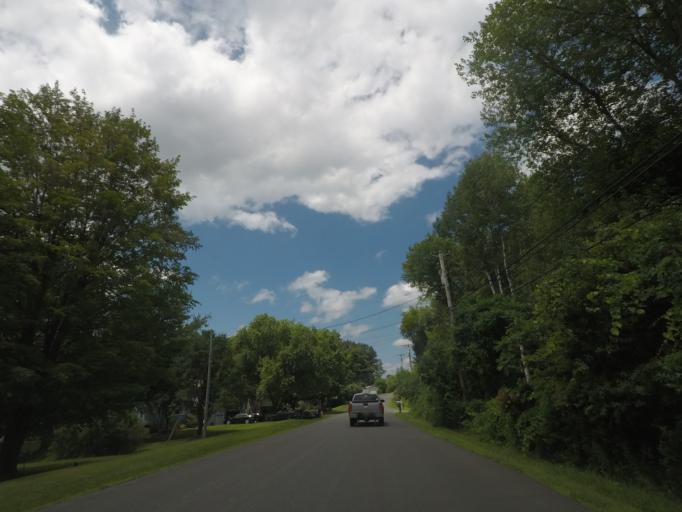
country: US
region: New York
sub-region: Rensselaer County
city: Castleton-on-Hudson
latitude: 42.5269
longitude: -73.6900
